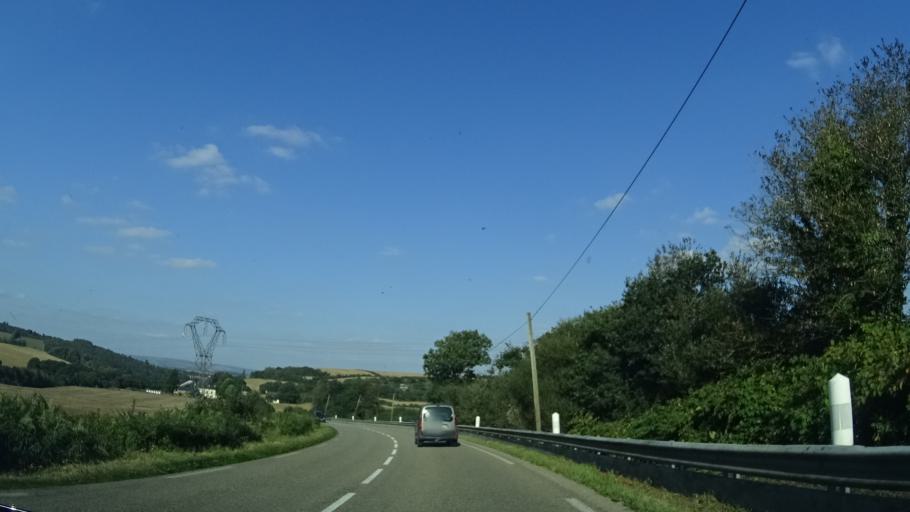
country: FR
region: Brittany
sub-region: Departement du Finistere
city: Chateaulin
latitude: 48.1806
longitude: -4.1119
